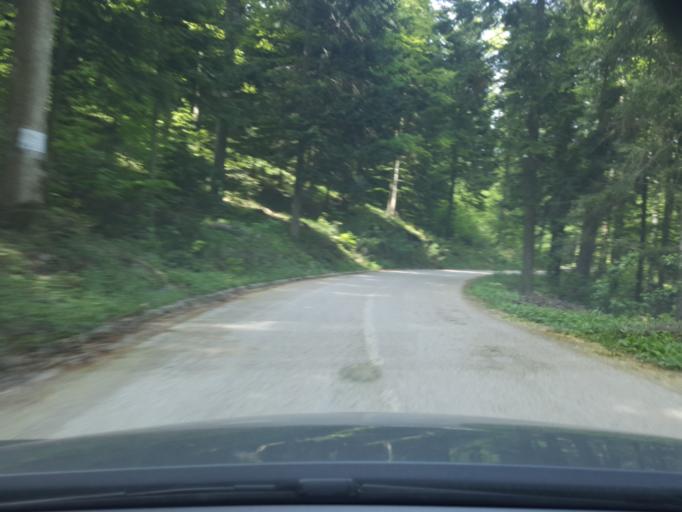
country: RS
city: Durici
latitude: 43.9295
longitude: 19.4501
